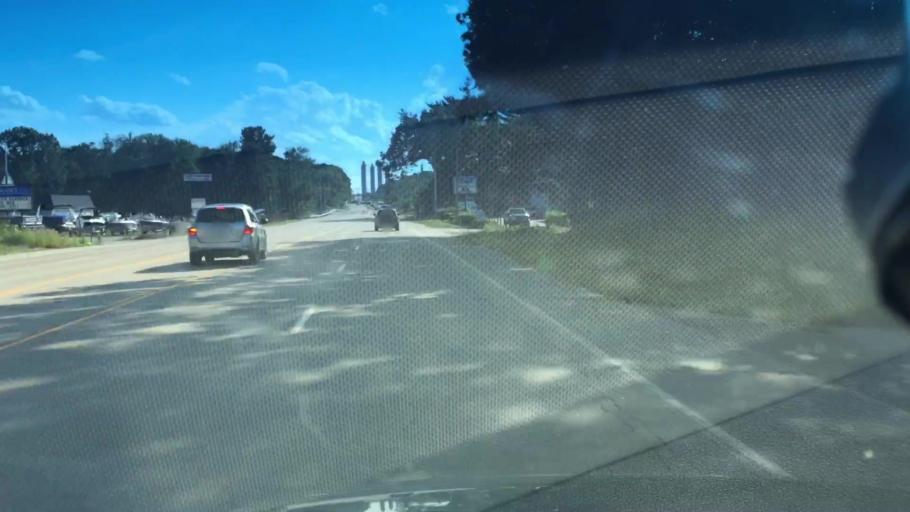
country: US
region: Maine
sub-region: York County
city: Kittery
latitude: 43.0952
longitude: -70.7516
